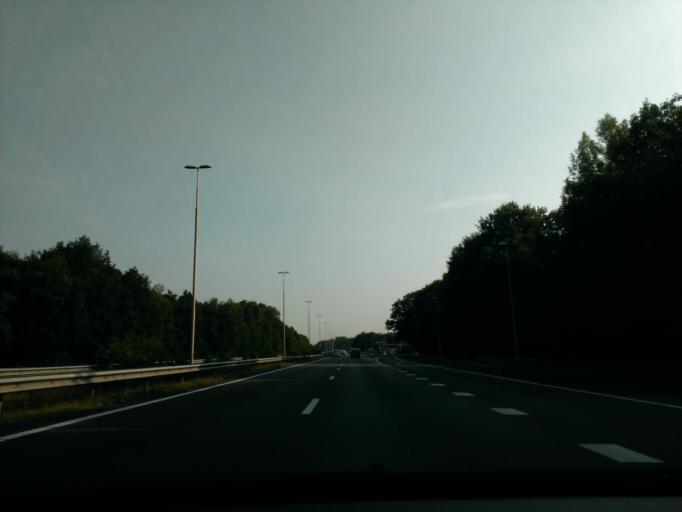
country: NL
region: Gelderland
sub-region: Gemeente Heerde
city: Heerde
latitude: 52.3989
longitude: 6.0146
